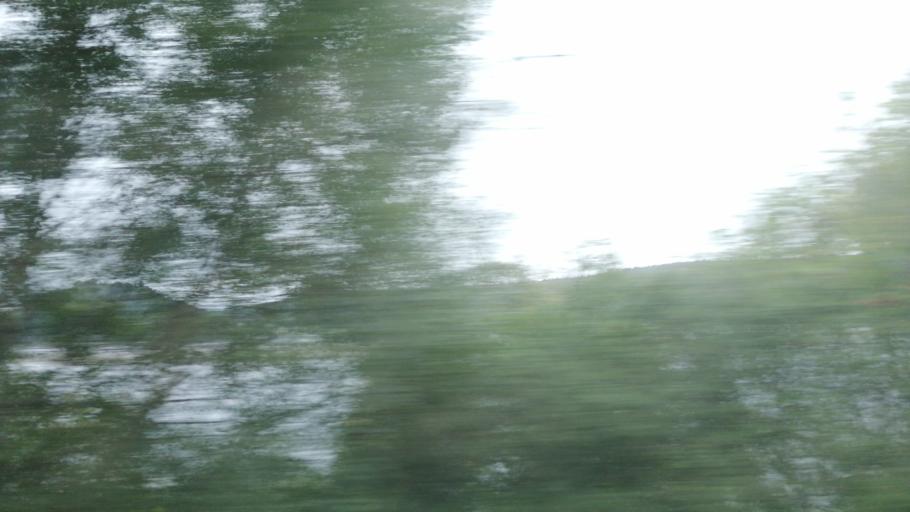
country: GB
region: Scotland
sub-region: Highland
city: Alness
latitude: 57.8556
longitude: -4.2544
